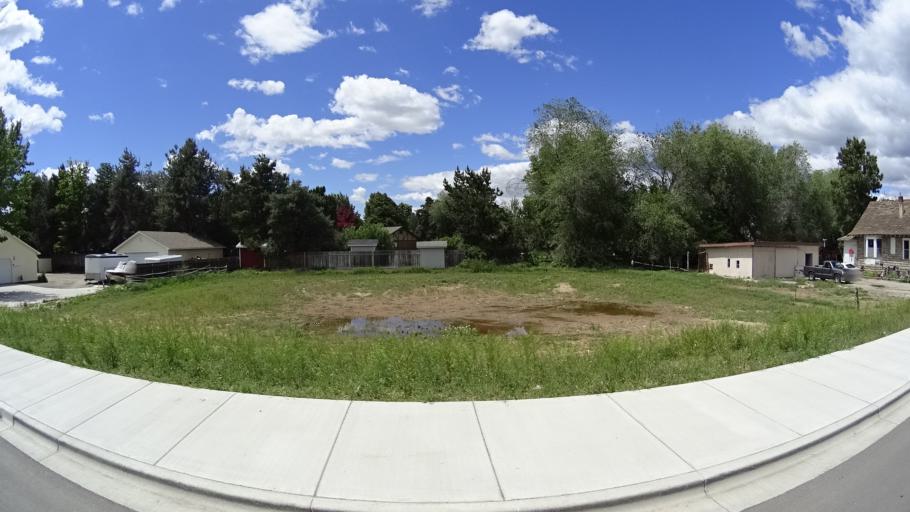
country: US
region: Idaho
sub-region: Ada County
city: Eagle
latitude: 43.6396
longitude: -116.3344
